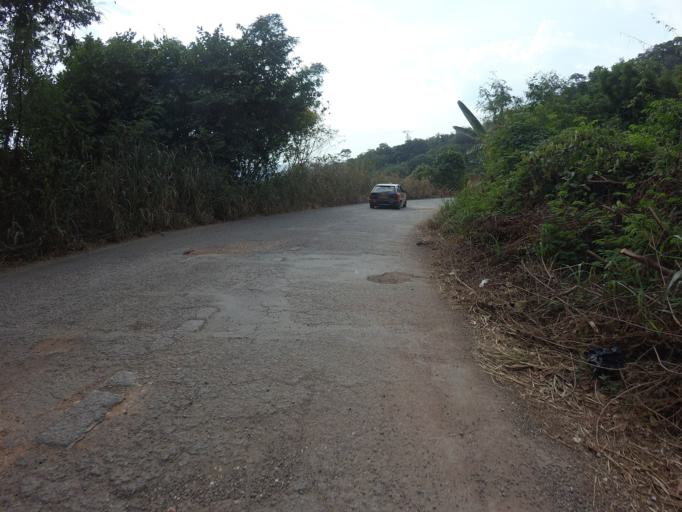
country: GH
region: Volta
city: Ho
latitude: 6.6825
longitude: 0.3428
